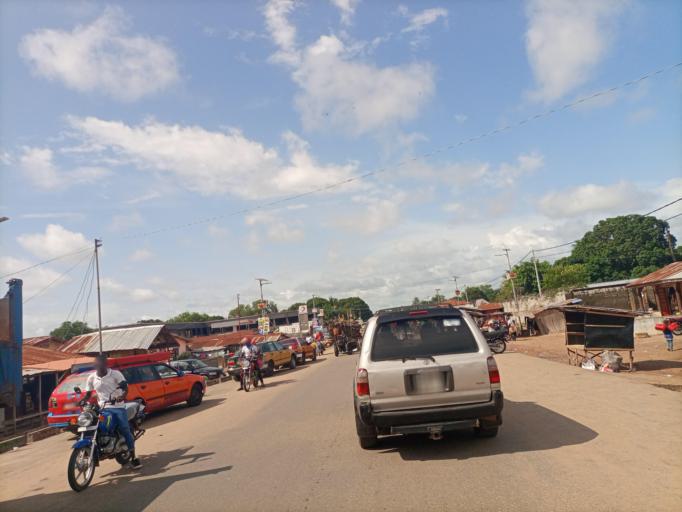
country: SL
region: Northern Province
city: Masoyila
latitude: 8.6054
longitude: -13.1799
